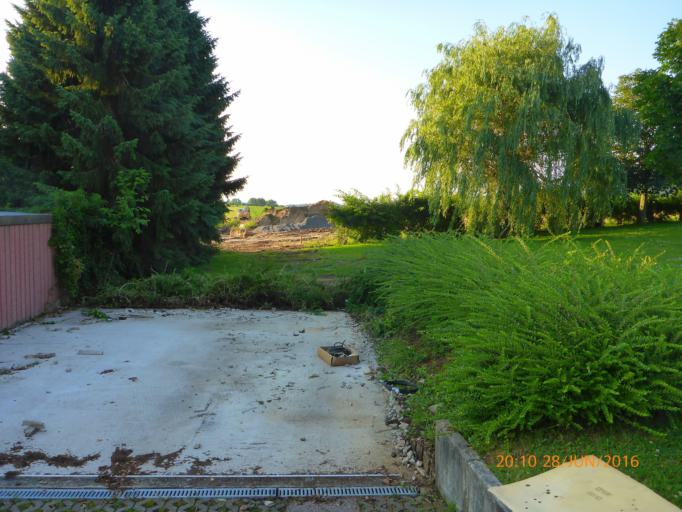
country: DE
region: Lower Saxony
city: Lauenau
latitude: 52.2793
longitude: 9.3736
